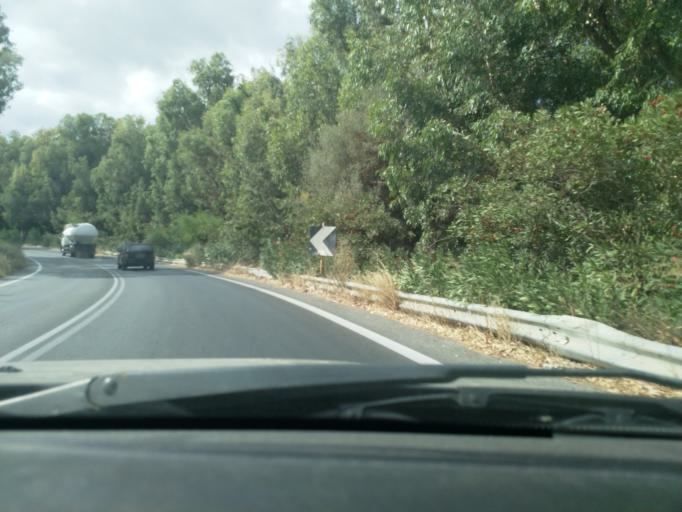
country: GR
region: Crete
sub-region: Nomos Chanias
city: Georgioupolis
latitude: 35.3617
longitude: 24.2570
